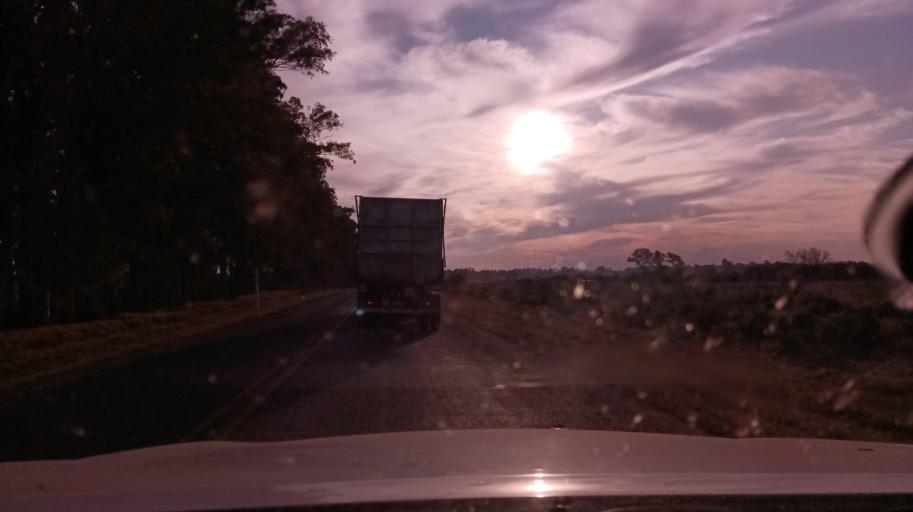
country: UY
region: Florida
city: Florida
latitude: -34.1413
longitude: -56.1643
